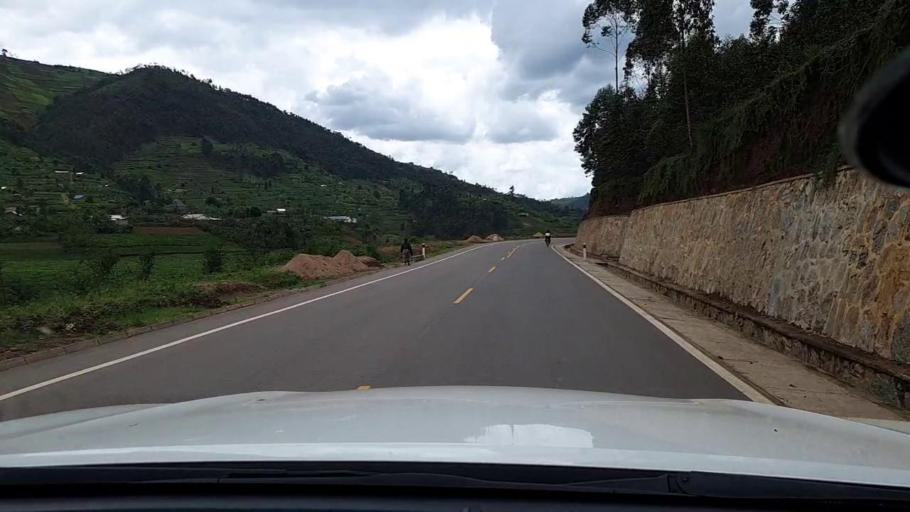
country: RW
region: Northern Province
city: Byumba
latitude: -1.6433
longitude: 29.8973
